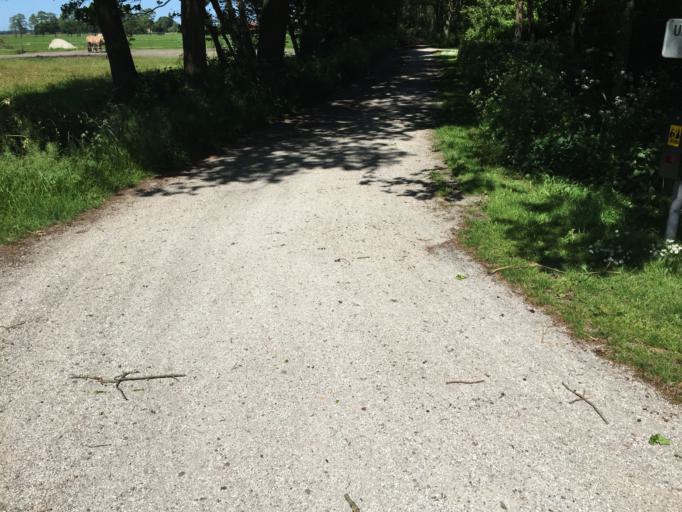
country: NL
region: Friesland
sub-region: Gemeente Smallingerland
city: Boornbergum
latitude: 53.0971
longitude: 6.0266
